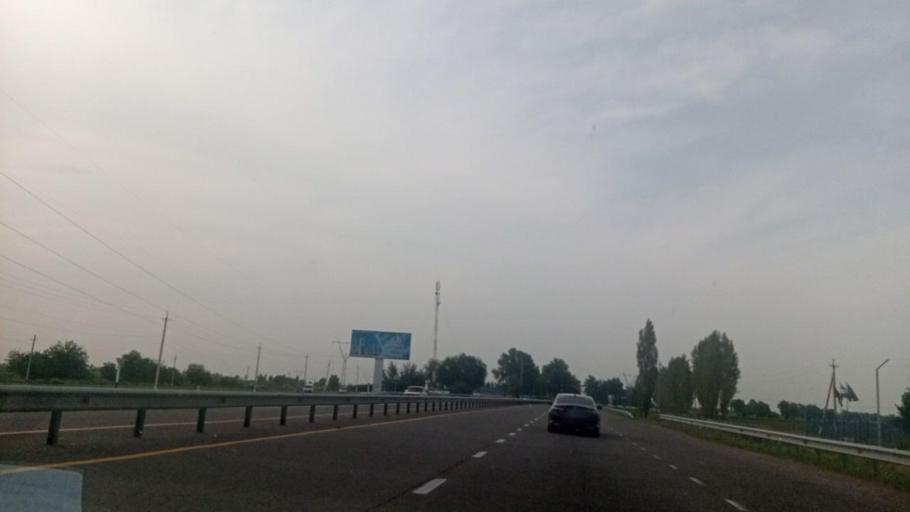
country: UZ
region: Toshkent Shahri
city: Bektemir
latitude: 41.1828
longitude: 69.4059
